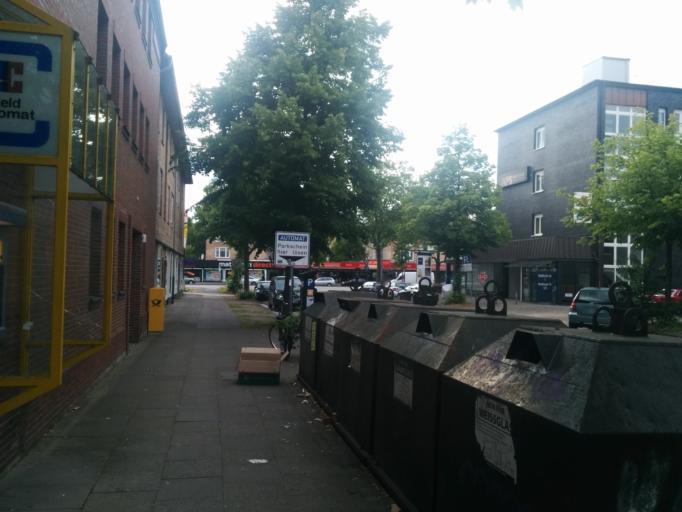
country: DE
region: Hamburg
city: Borgfelde
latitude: 53.5771
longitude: 10.0397
